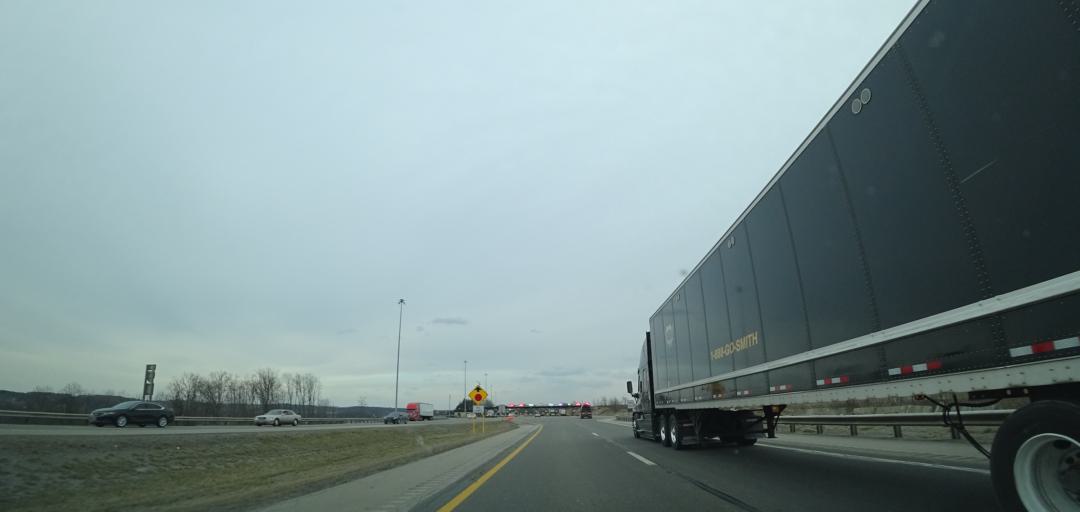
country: US
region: Ohio
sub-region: Mahoning County
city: New Middletown
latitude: 40.9255
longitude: -80.5599
